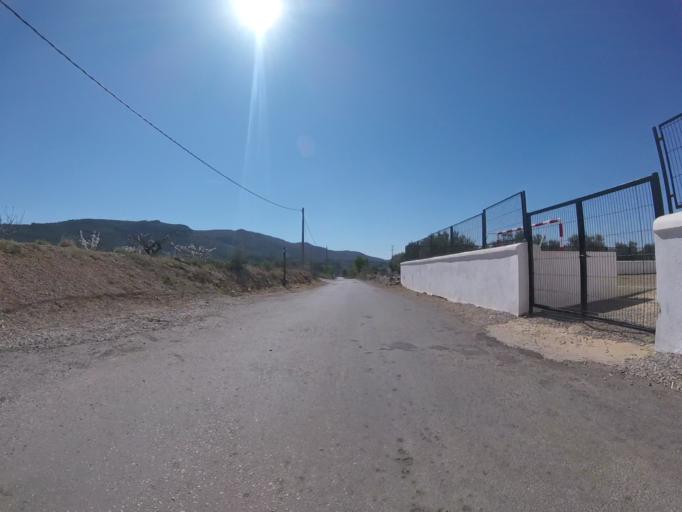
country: ES
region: Valencia
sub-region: Provincia de Castello
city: Chert/Xert
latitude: 40.4157
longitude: 0.1750
